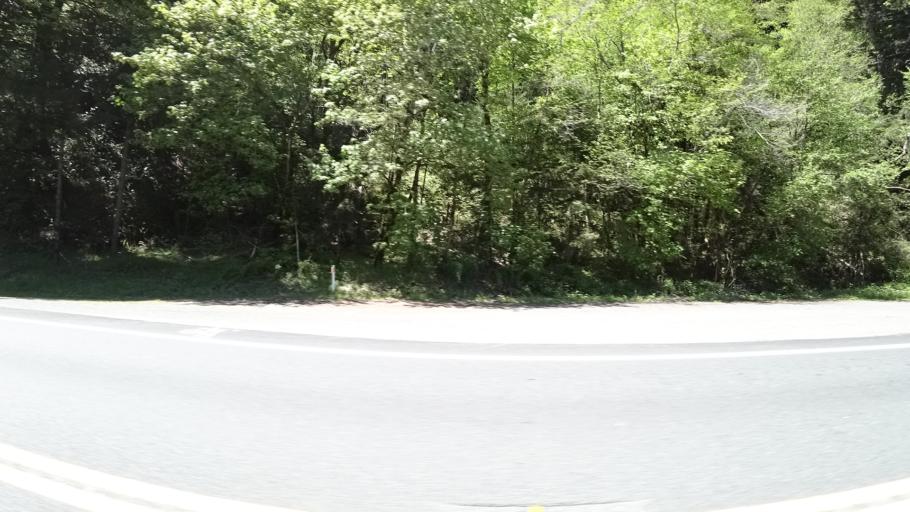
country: US
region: California
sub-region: Humboldt County
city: Willow Creek
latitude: 40.9291
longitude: -123.6885
